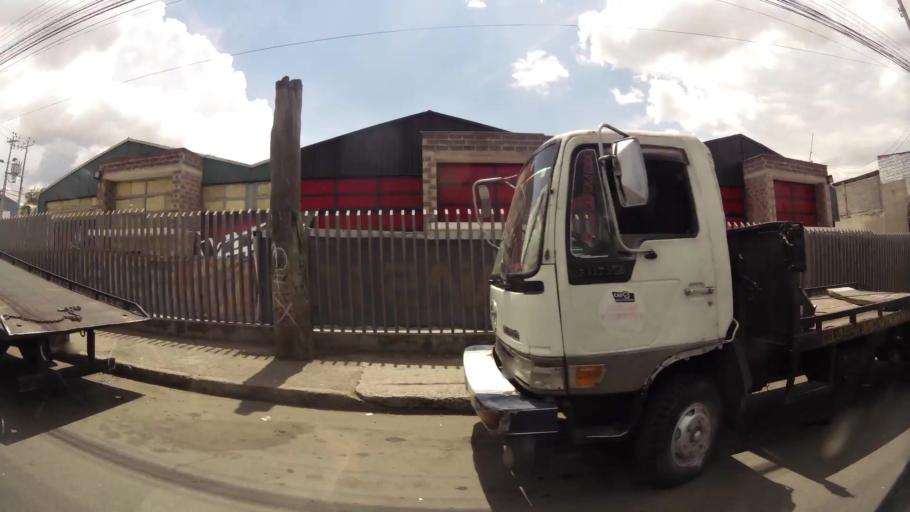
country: EC
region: Pichincha
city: Quito
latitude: -0.1079
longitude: -78.4504
